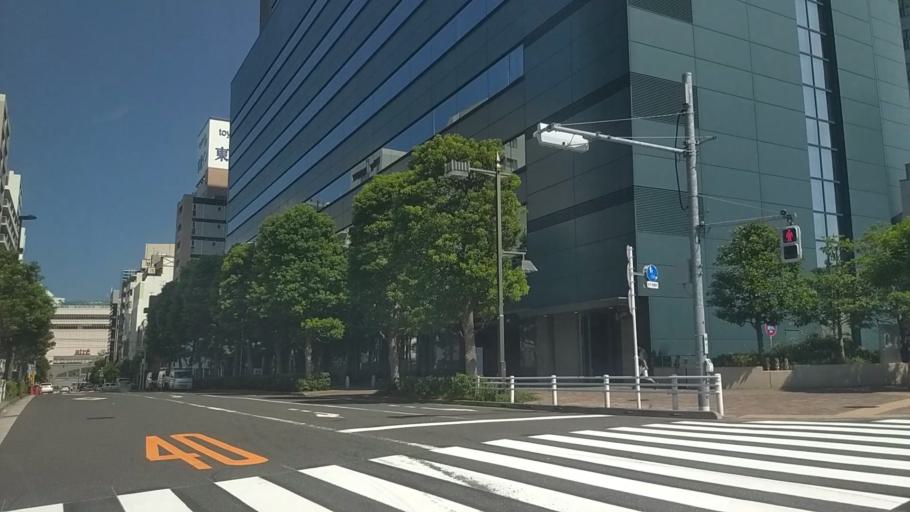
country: JP
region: Kanagawa
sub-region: Kawasaki-shi
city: Kawasaki
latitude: 35.6065
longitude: 139.7300
